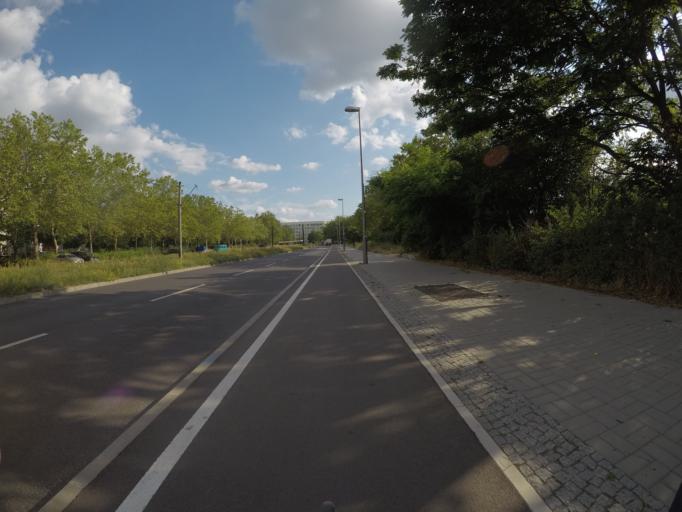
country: DE
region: Berlin
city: Marzahn
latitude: 52.5476
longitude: 13.5864
